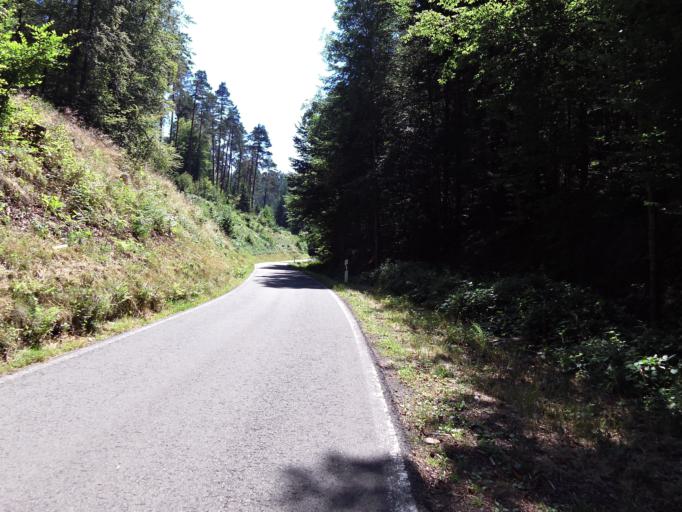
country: DE
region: Rheinland-Pfalz
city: Elmstein
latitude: 49.3841
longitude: 7.9177
